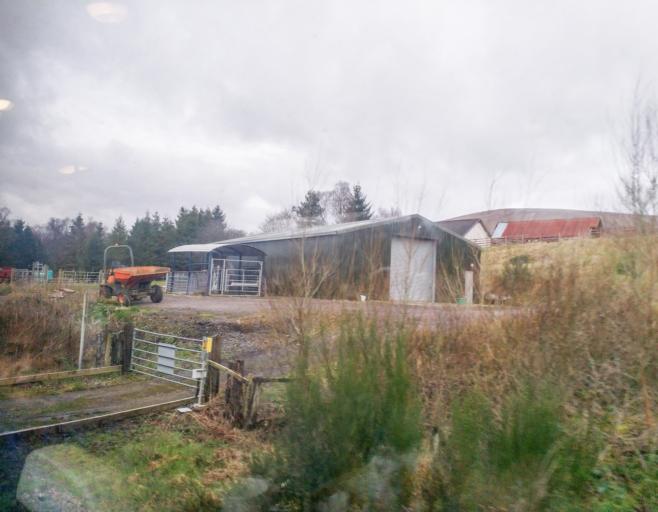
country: GB
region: Scotland
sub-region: Highland
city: Spean Bridge
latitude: 56.8893
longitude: -4.8687
